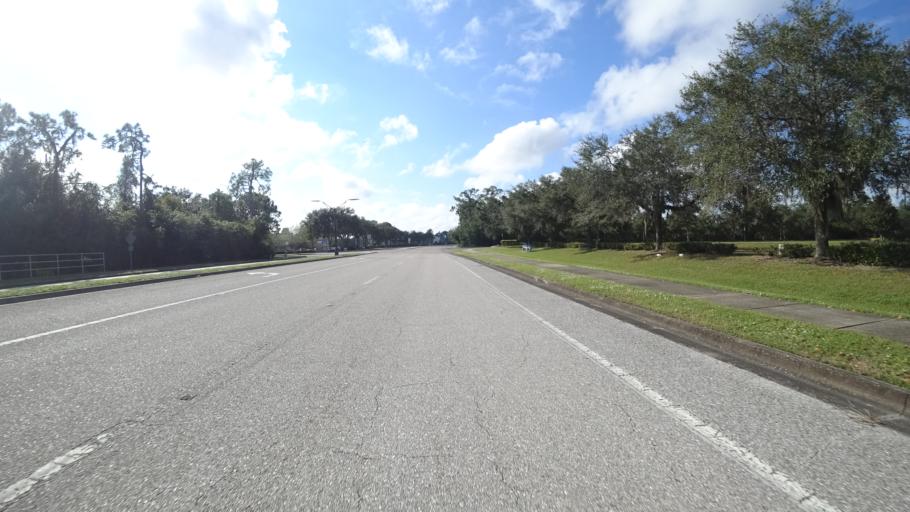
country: US
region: Florida
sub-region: Sarasota County
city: The Meadows
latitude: 27.3928
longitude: -82.4631
